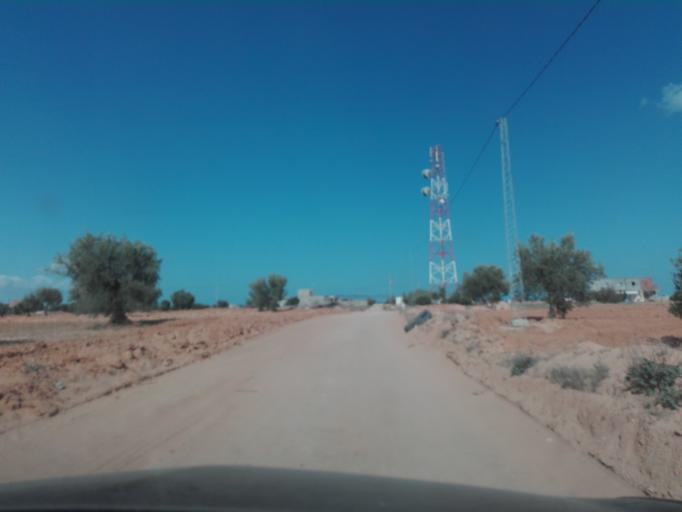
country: TN
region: Madanin
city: Bin Qirdan
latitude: 33.1677
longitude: 11.1966
